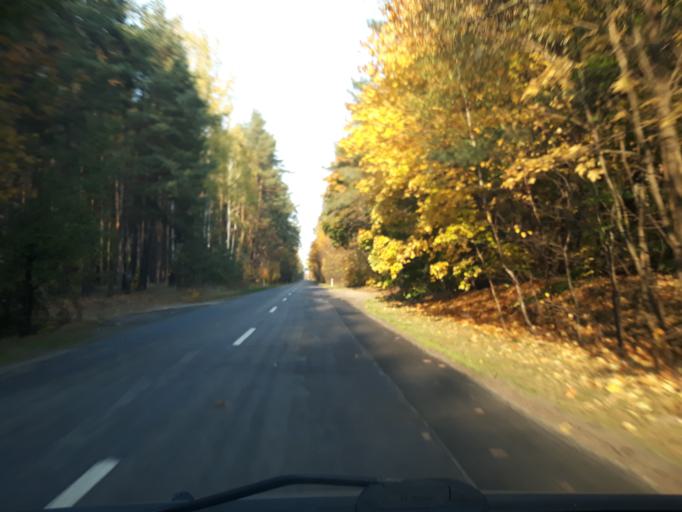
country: PL
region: Pomeranian Voivodeship
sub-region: Powiat chojnicki
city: Chojnice
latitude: 53.6430
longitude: 17.5085
